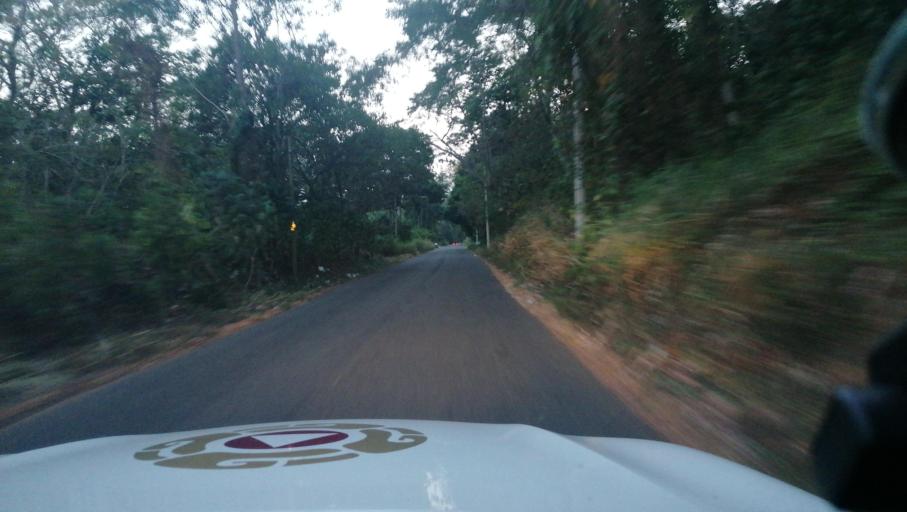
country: MX
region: Chiapas
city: Veinte de Noviembre
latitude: 15.0172
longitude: -92.2452
